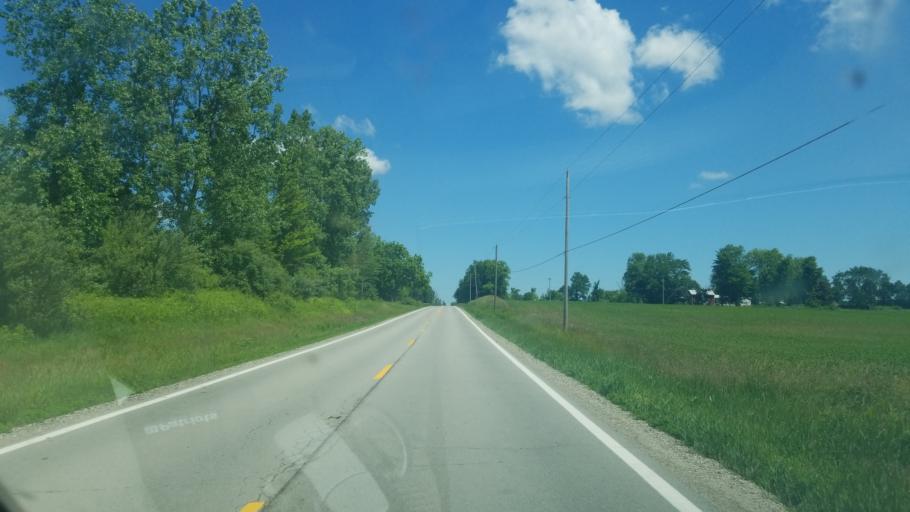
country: US
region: Ohio
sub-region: Huron County
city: New London
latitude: 41.1483
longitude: -82.4100
